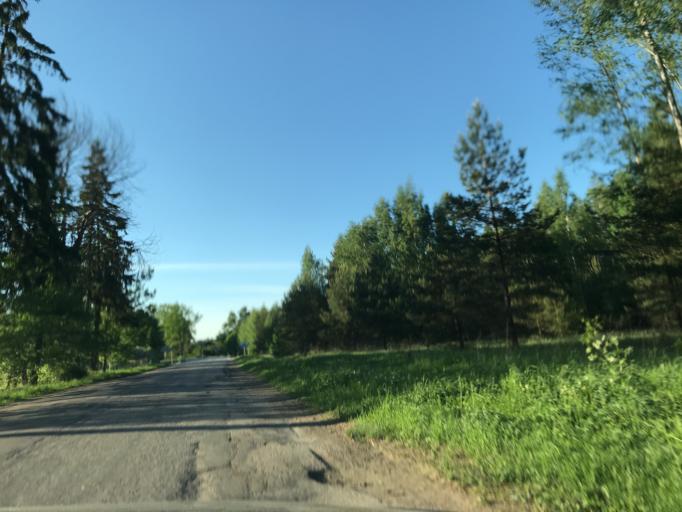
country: LV
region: Ozolnieku
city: Ozolnieki
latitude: 56.6085
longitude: 23.7893
